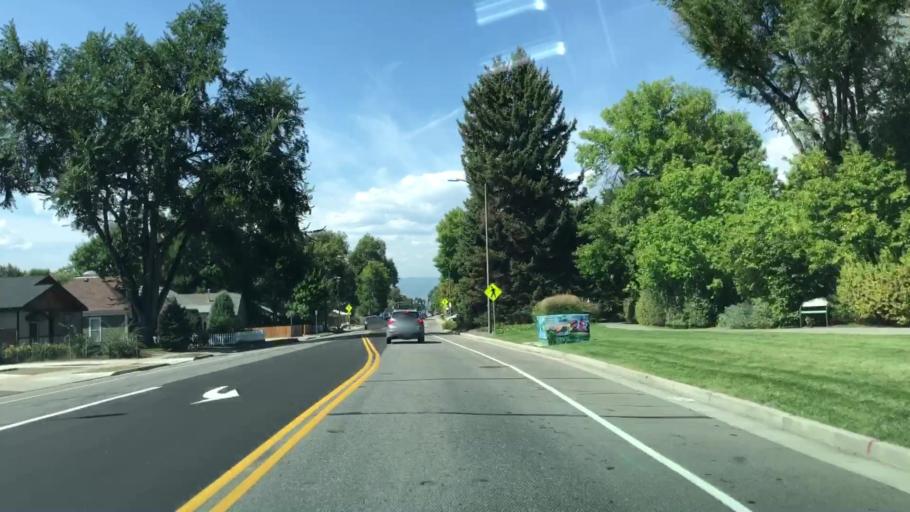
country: US
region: Colorado
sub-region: Larimer County
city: Loveland
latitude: 40.3928
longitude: -105.0691
